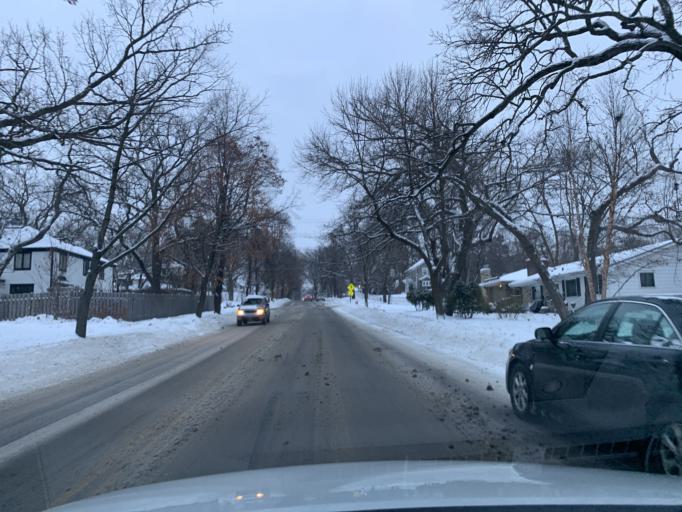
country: US
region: Minnesota
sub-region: Hennepin County
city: Saint Louis Park
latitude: 44.9241
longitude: -93.3412
